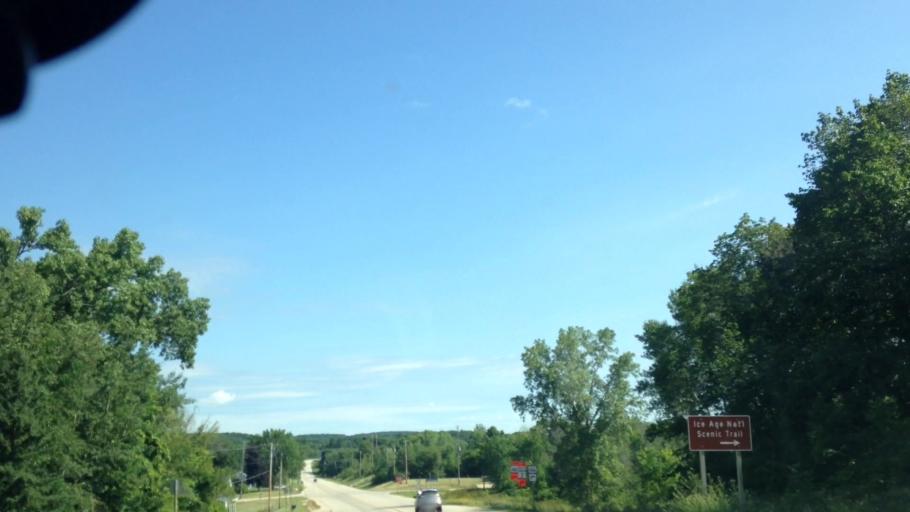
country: US
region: Wisconsin
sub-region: Washington County
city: Slinger
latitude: 43.3513
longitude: -88.2807
